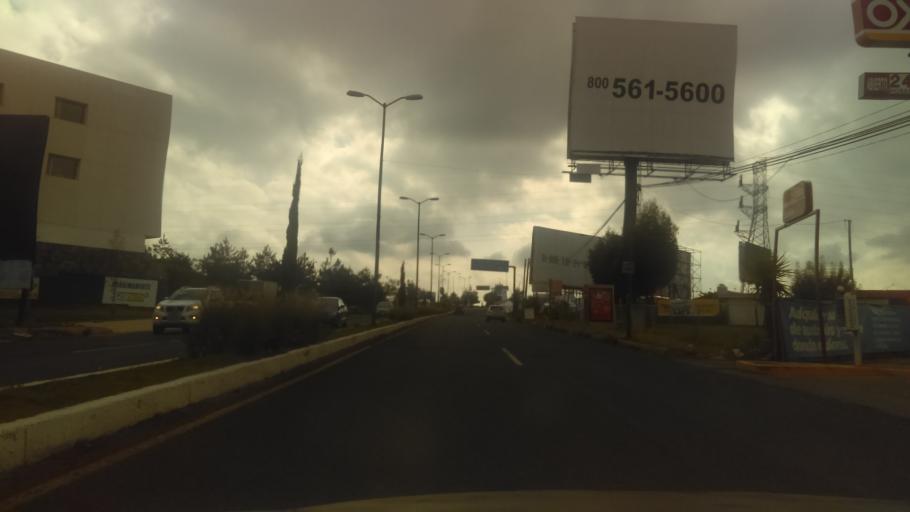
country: MX
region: Michoacan
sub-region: Morelia
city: Montana Monarca (Punta Altozano)
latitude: 19.6676
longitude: -101.1672
